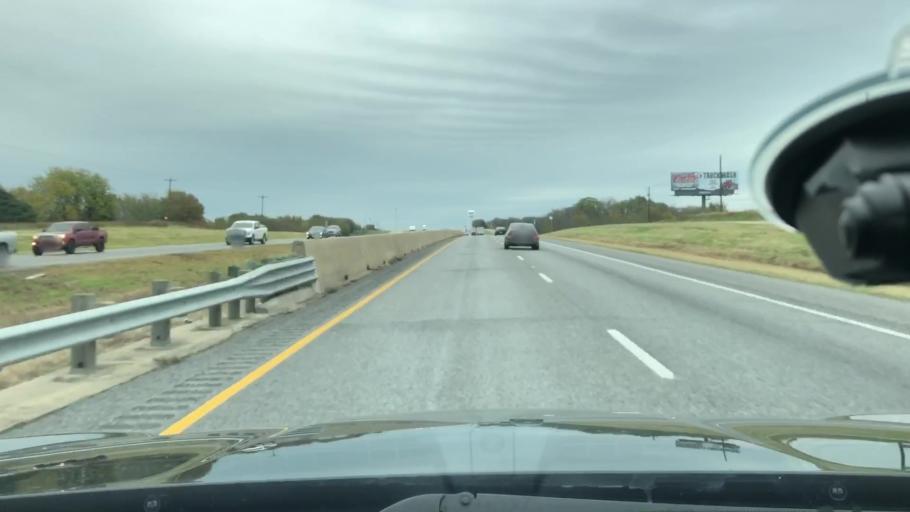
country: US
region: Texas
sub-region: Hunt County
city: Commerce
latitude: 33.1305
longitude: -95.8994
